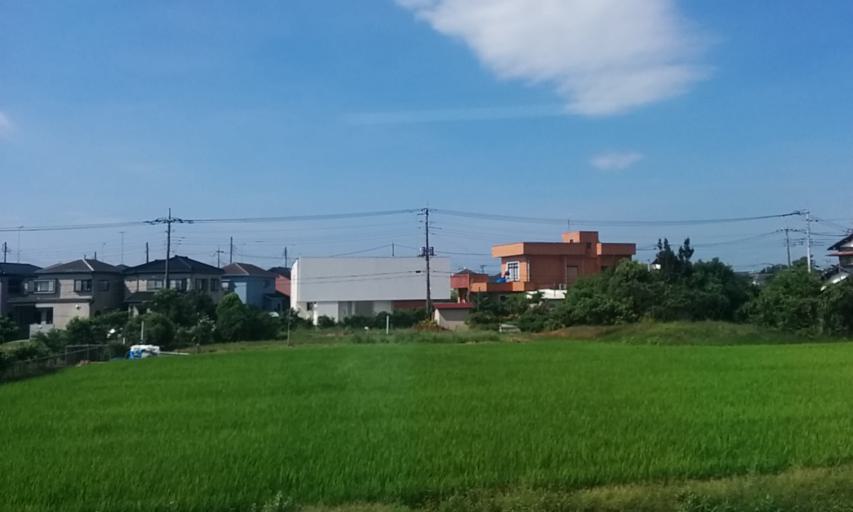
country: JP
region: Saitama
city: Kazo
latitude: 36.1279
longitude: 139.5881
